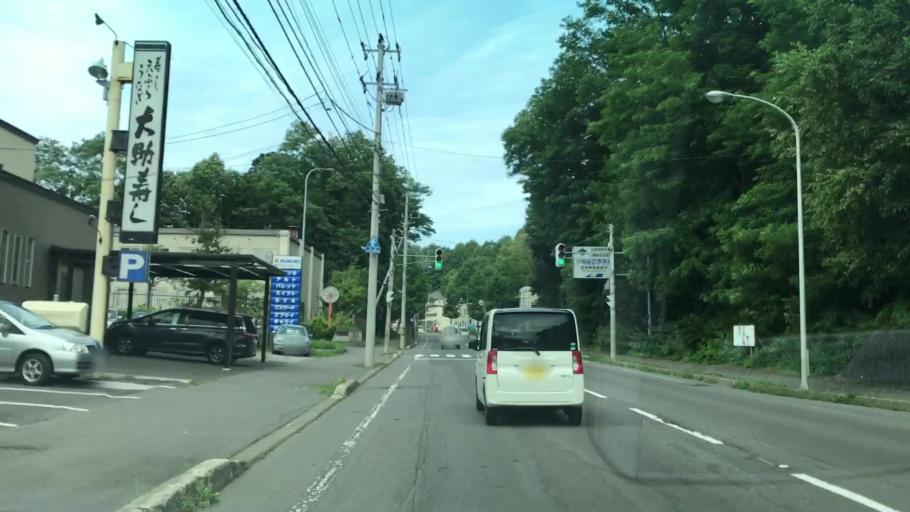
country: JP
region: Hokkaido
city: Otaru
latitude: 43.2108
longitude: 140.9677
